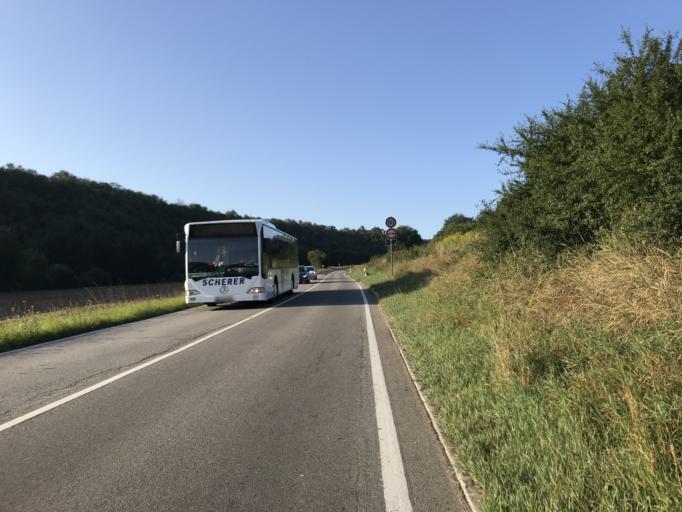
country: DE
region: Rheinland-Pfalz
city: Norheim
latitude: 49.8049
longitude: 7.8290
